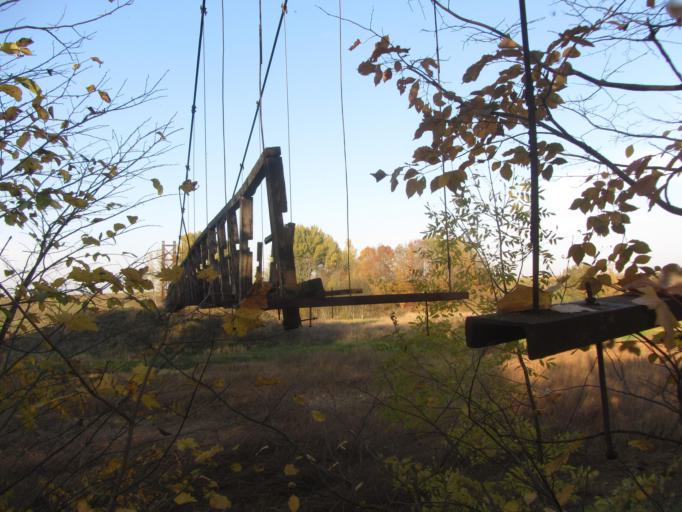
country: LT
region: Panevezys
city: Pasvalys
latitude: 56.0470
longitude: 24.1926
